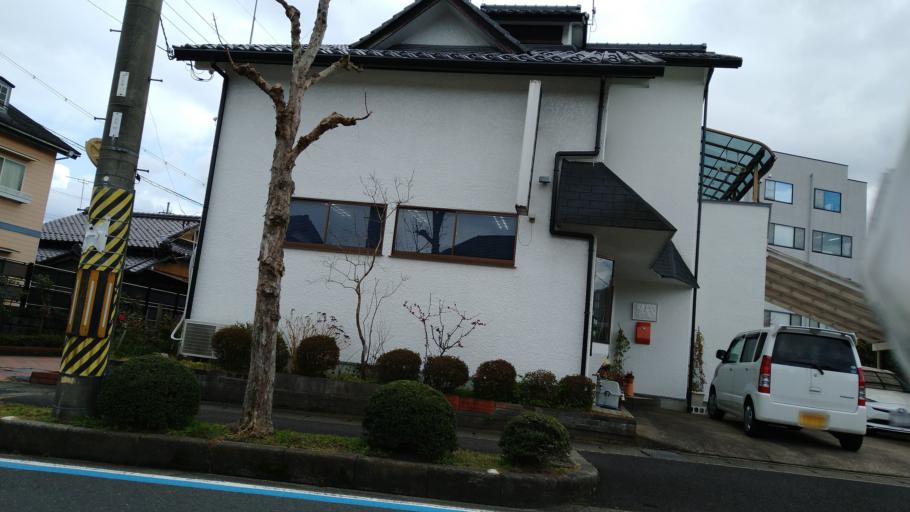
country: JP
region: Kyoto
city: Maizuru
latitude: 35.4564
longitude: 135.3969
